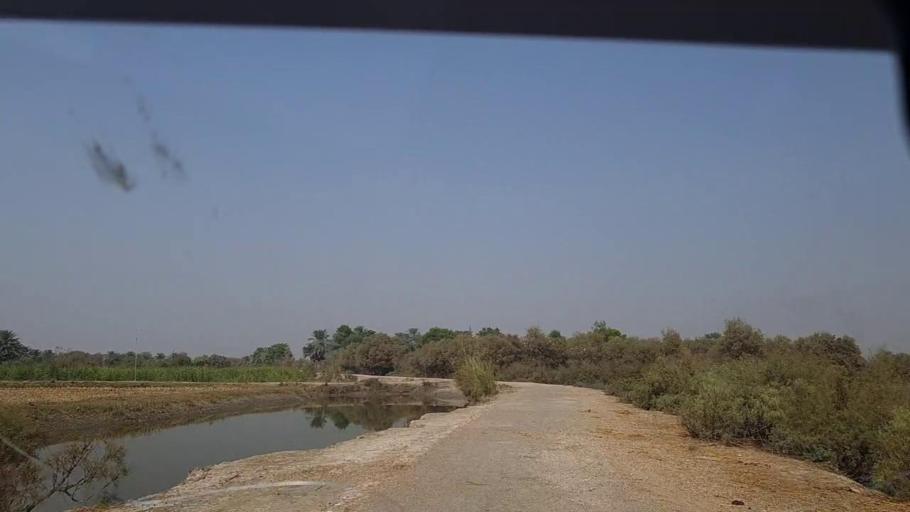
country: PK
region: Sindh
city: Shikarpur
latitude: 28.0884
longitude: 68.6696
